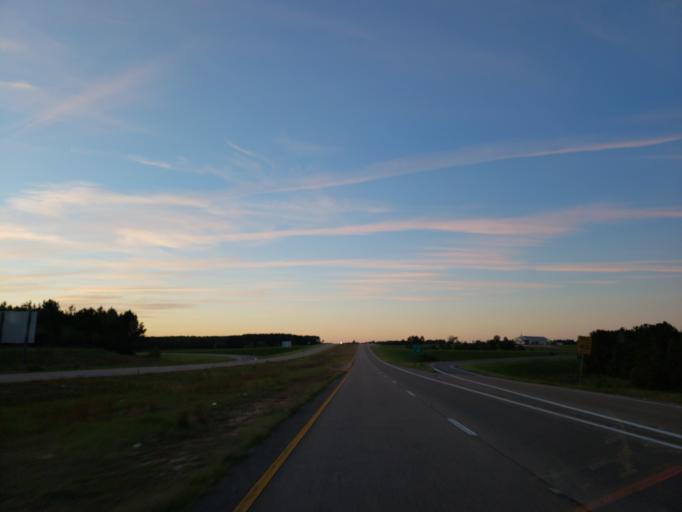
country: US
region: Mississippi
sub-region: Wayne County
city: Waynesboro
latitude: 31.7036
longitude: -88.6229
